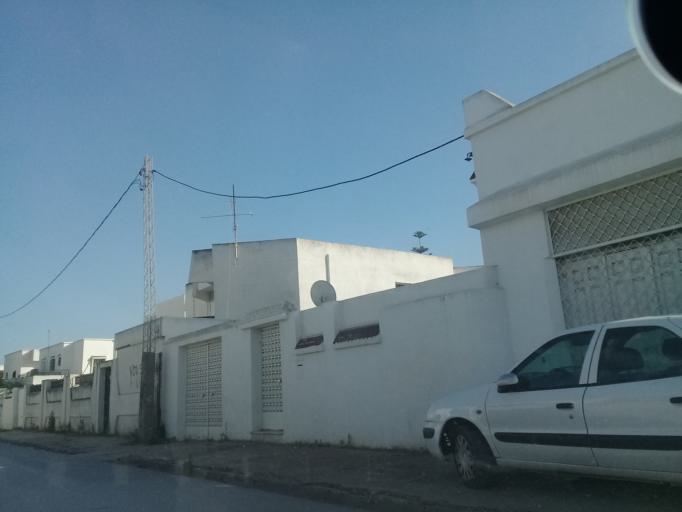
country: TN
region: Ariana
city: Ariana
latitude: 36.8353
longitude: 10.1964
